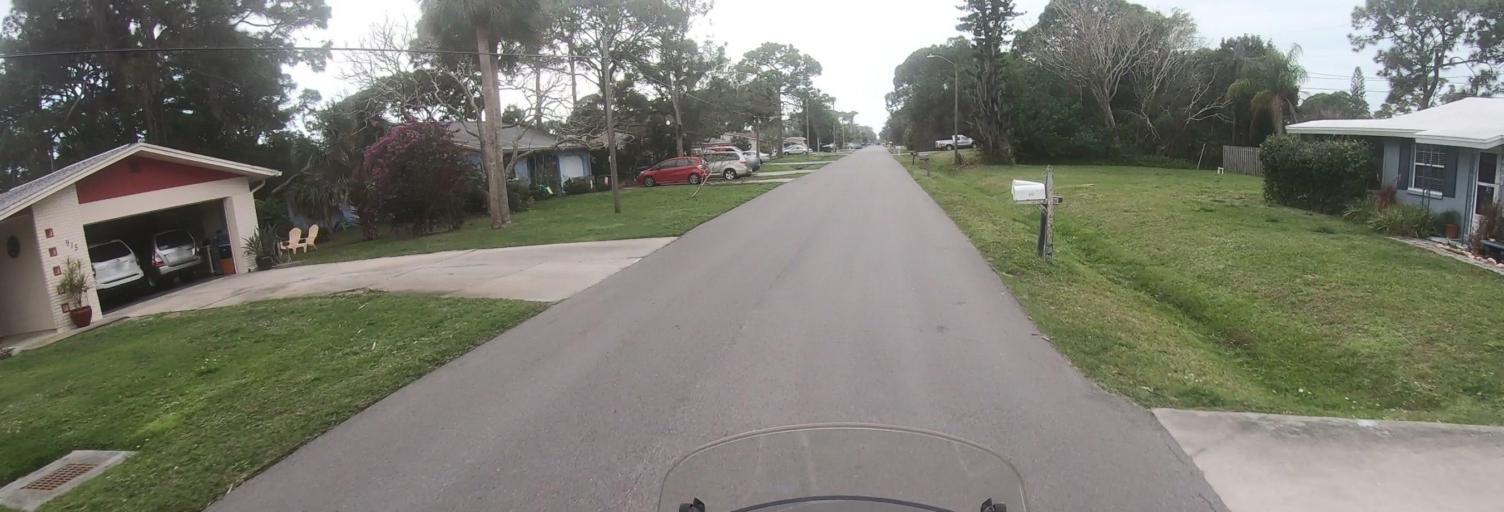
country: US
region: Florida
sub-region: Sarasota County
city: South Venice
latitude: 27.0599
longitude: -82.4277
